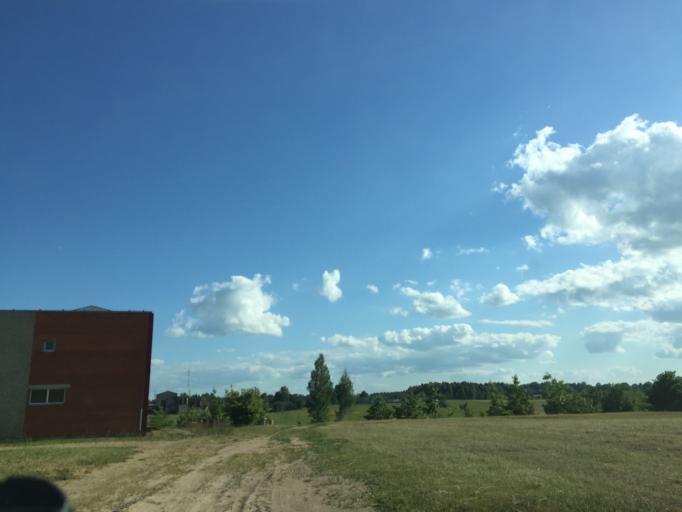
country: LV
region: Skriveri
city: Skriveri
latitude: 56.8483
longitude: 25.1460
